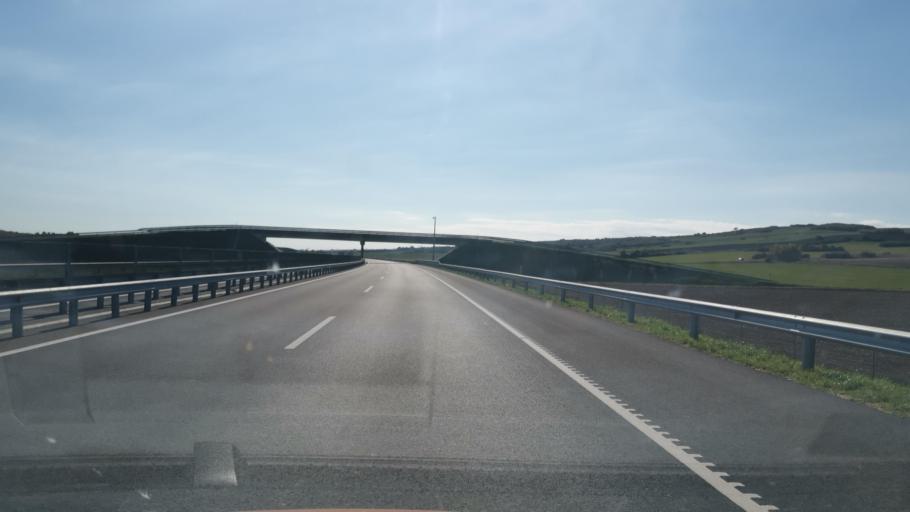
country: HU
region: Borsod-Abauj-Zemplen
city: Szikszo
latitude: 48.1967
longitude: 20.9067
